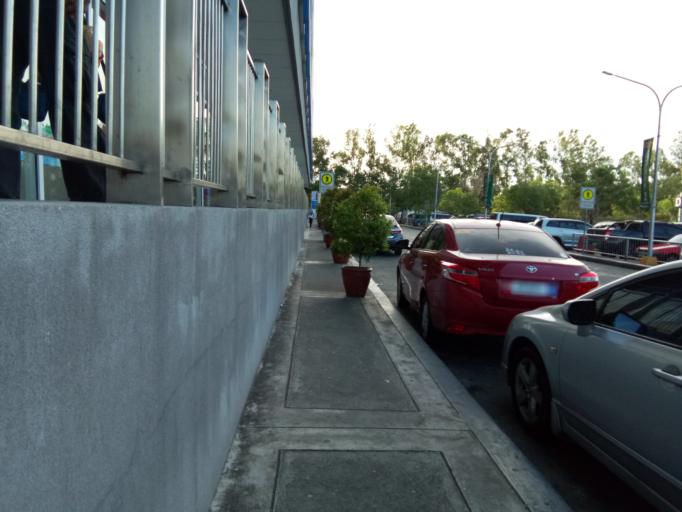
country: PH
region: Calabarzon
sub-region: Province of Cavite
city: Dasmarinas
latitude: 14.3022
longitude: 120.9569
